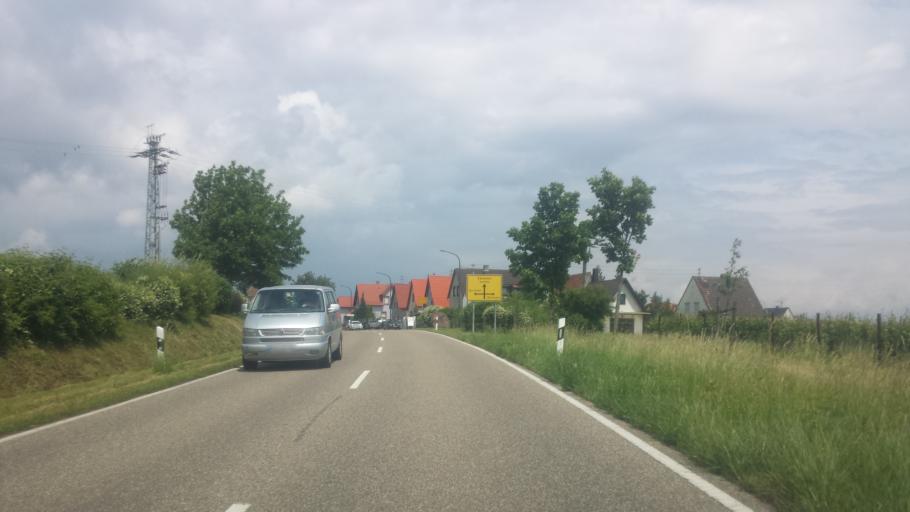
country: DE
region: Rheinland-Pfalz
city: Burrweiler
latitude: 49.2452
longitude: 8.0773
